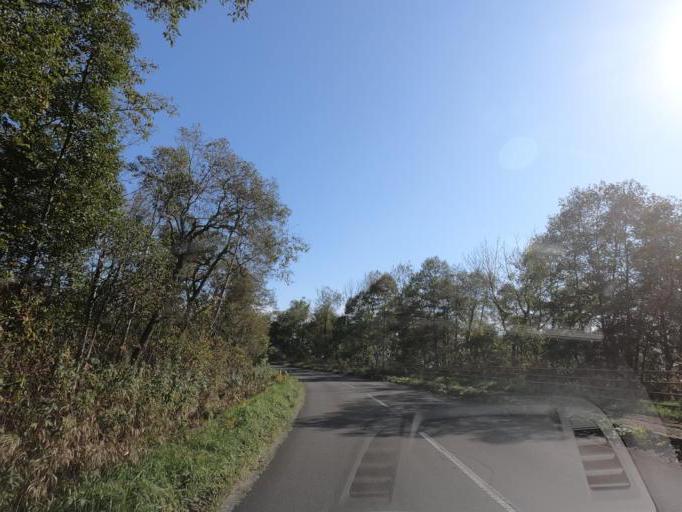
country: JP
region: Hokkaido
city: Obihiro
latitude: 42.6103
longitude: 143.5448
